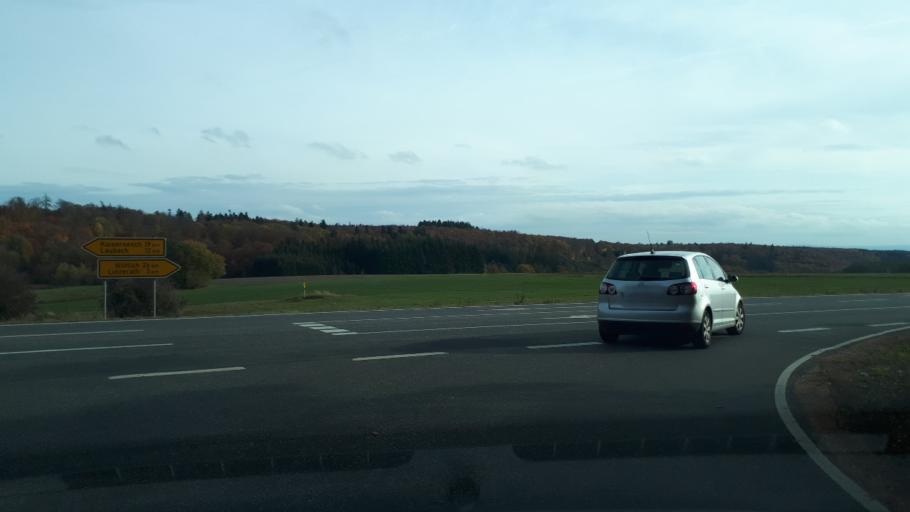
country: DE
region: Rheinland-Pfalz
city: Gillenbeuren
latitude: 50.1518
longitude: 7.0332
